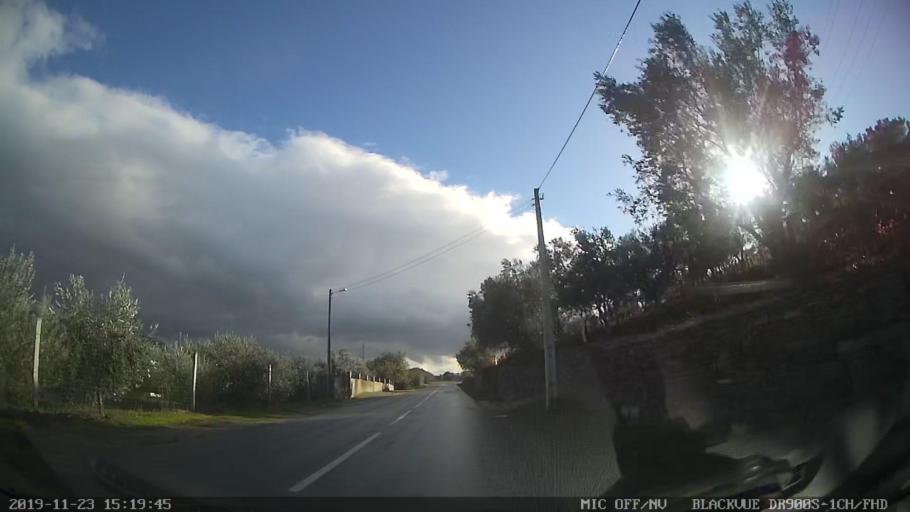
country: PT
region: Viseu
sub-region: Lamego
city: Lamego
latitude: 41.1156
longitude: -7.7903
